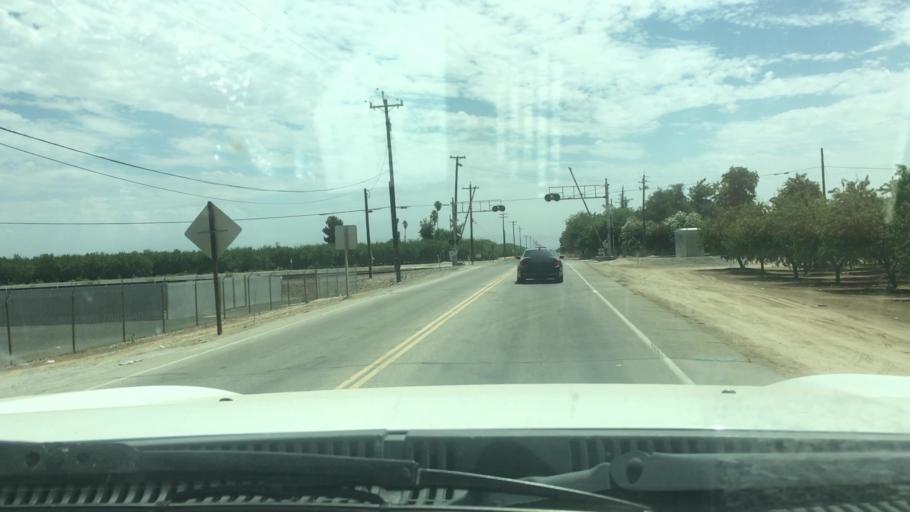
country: US
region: California
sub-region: Kern County
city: Wasco
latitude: 35.5580
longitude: -119.3313
